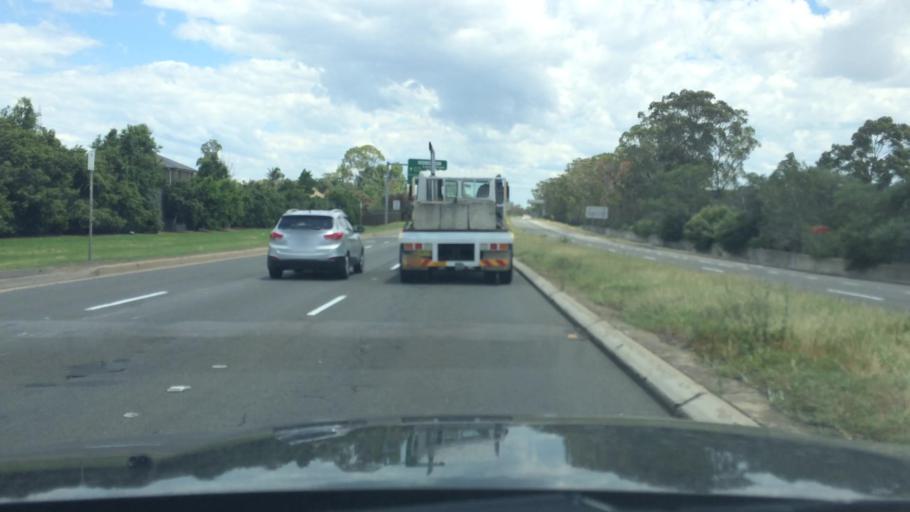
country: AU
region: New South Wales
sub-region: Campbelltown Municipality
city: Glenfield
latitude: -33.9610
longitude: 150.8834
